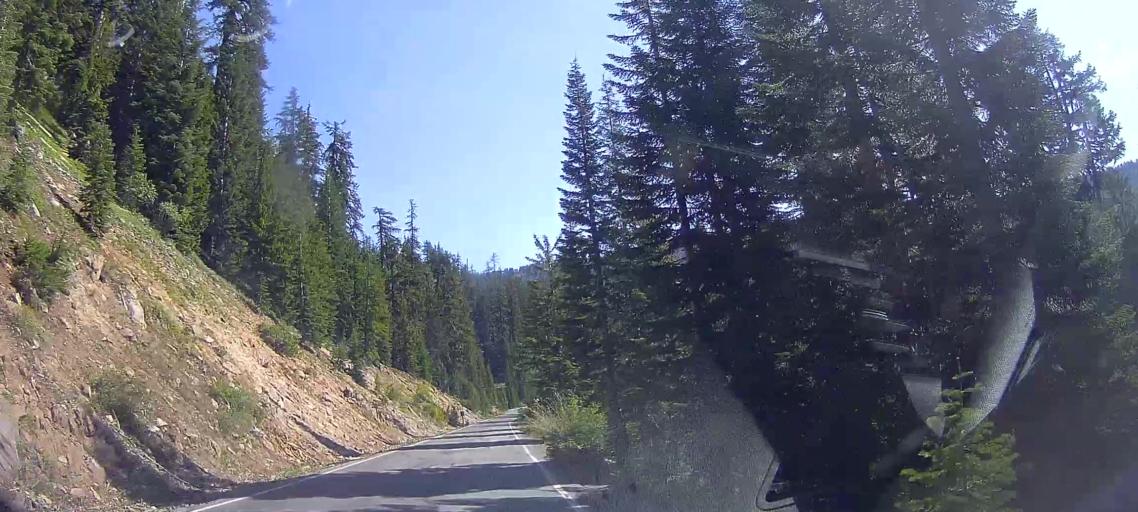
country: US
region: Oregon
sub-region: Klamath County
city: Klamath Falls
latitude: 42.8823
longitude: -122.1011
